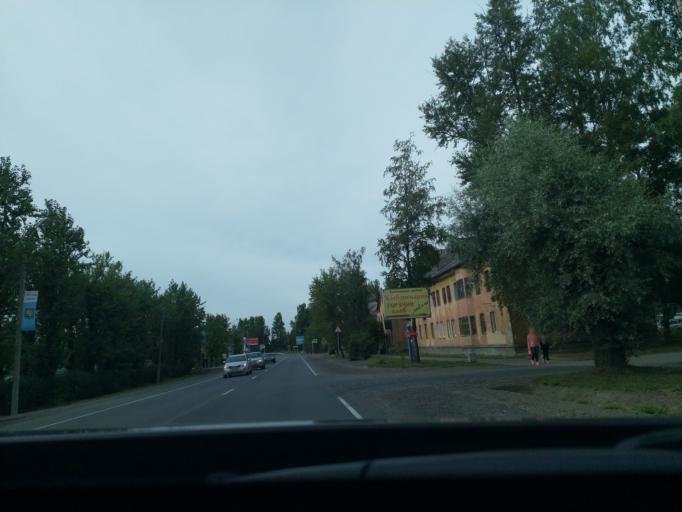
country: RU
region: Leningrad
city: Nikol'skoye
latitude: 59.7061
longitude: 30.7844
